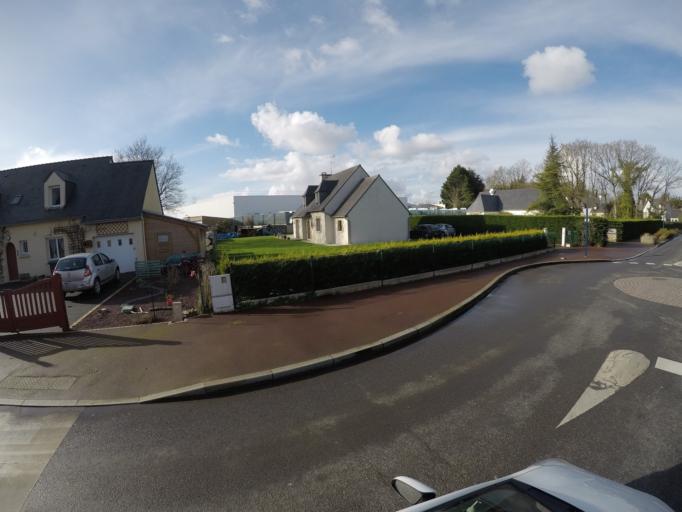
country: FR
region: Brittany
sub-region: Departement des Cotes-d'Armor
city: Lanvollon
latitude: 48.6367
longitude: -2.9871
